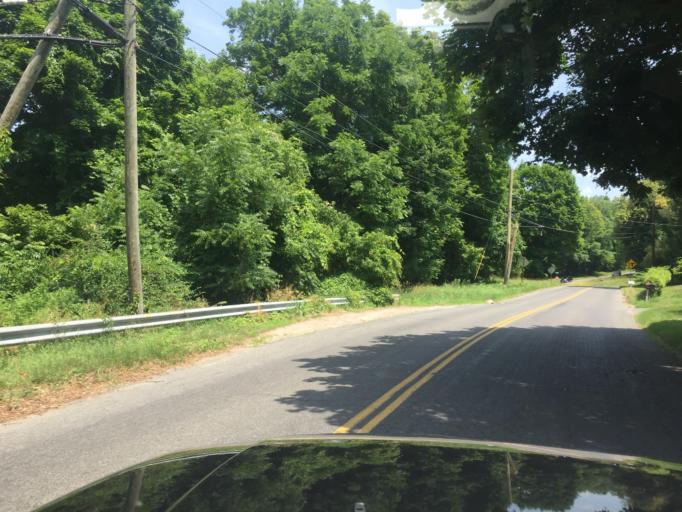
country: US
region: Connecticut
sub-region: Litchfield County
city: New Milford
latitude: 41.5406
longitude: -73.4113
